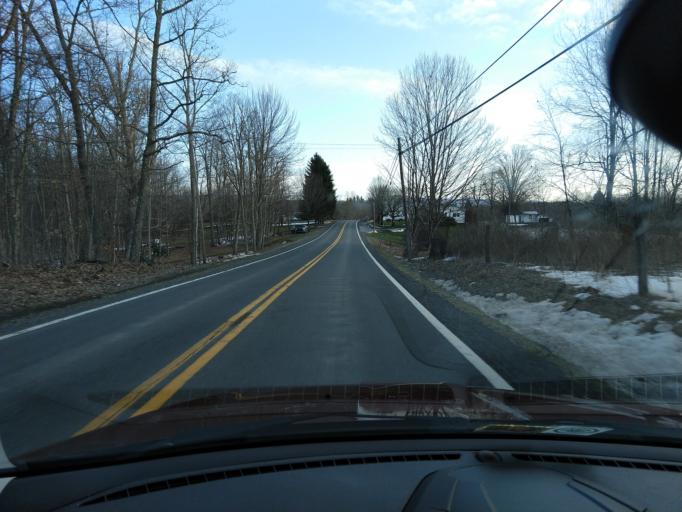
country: US
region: West Virginia
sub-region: Pocahontas County
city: Marlinton
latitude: 38.1039
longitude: -80.2753
